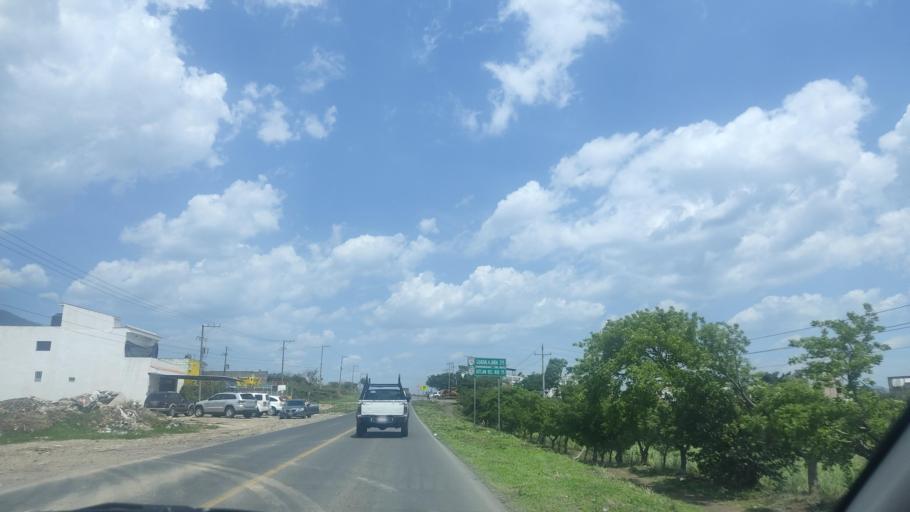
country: MX
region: Nayarit
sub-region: Tepic
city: La Corregidora
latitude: 21.4468
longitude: -104.8115
